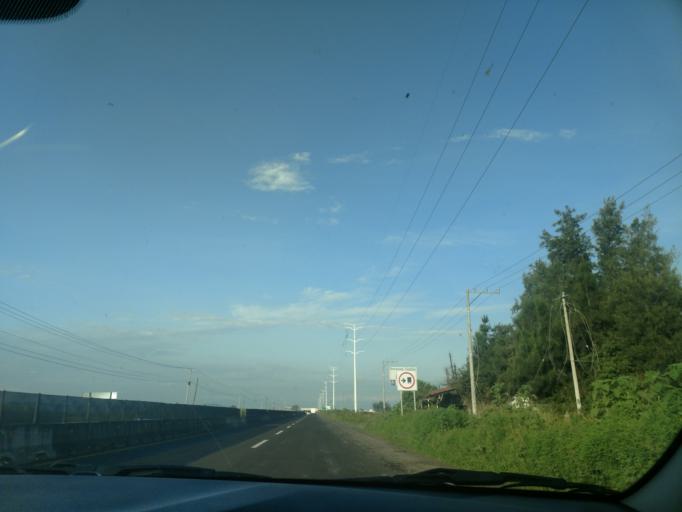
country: MX
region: Jalisco
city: El Refugio
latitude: 20.6531
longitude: -103.7409
